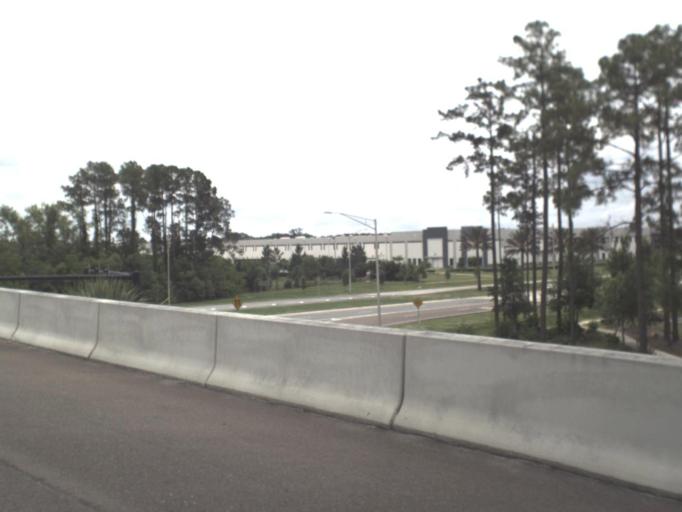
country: US
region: Florida
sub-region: Nassau County
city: Nassau Village-Ratliff
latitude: 30.4849
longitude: -81.6656
